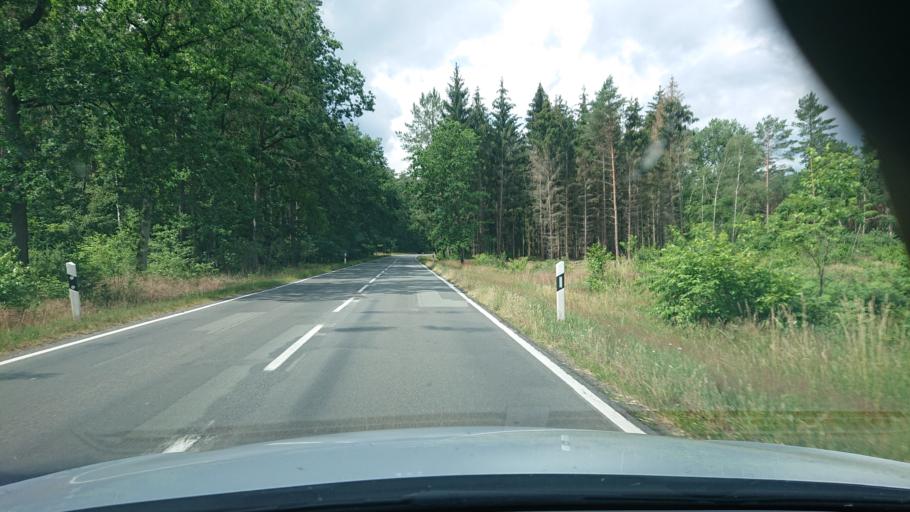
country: DE
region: Mecklenburg-Vorpommern
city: Ludwigslust
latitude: 53.3592
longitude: 11.4772
